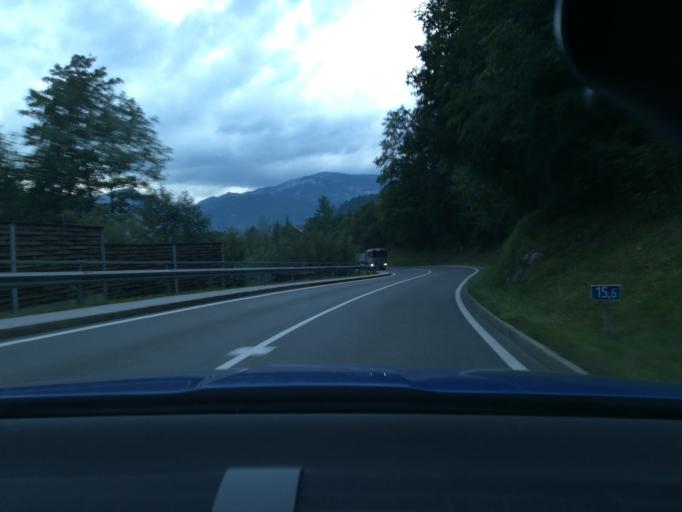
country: AT
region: Salzburg
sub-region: Politischer Bezirk Hallein
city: Abtenau
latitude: 47.5715
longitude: 13.3318
